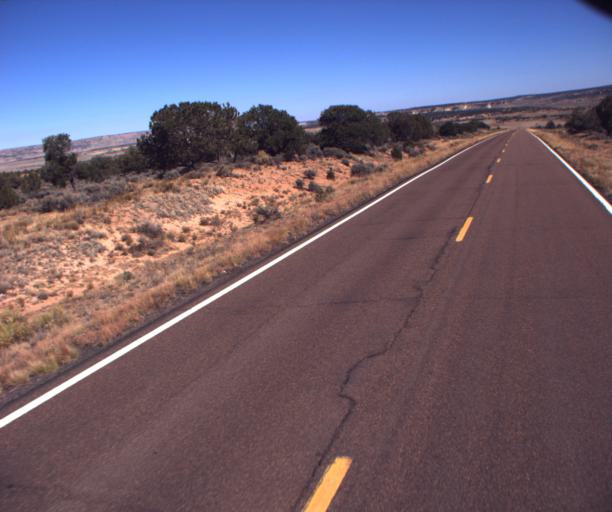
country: US
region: Arizona
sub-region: Apache County
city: Ganado
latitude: 35.7520
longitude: -109.9052
